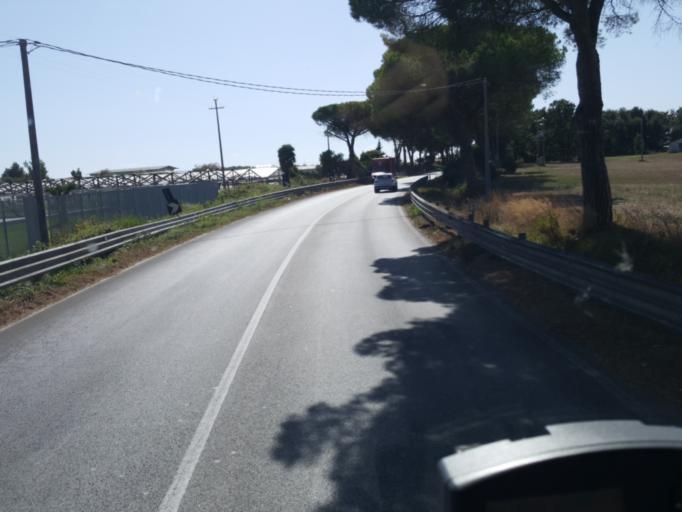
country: IT
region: Latium
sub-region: Provincia di Latina
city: Genio Civile
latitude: 41.5141
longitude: 12.7014
